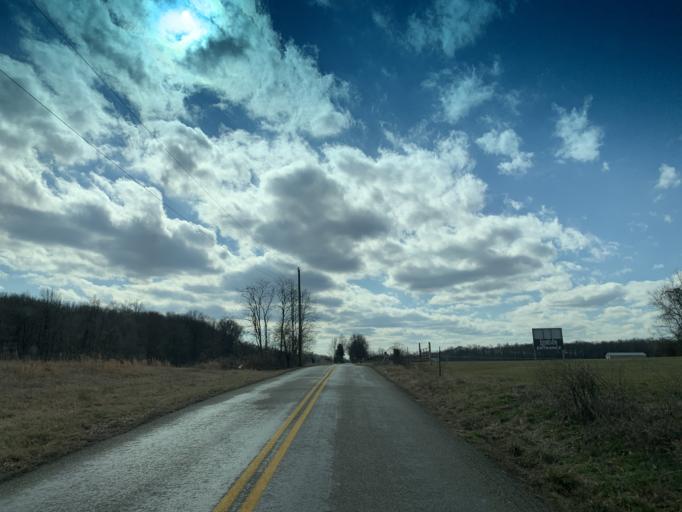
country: US
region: Maryland
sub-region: Harford County
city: Aberdeen
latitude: 39.5602
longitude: -76.2000
